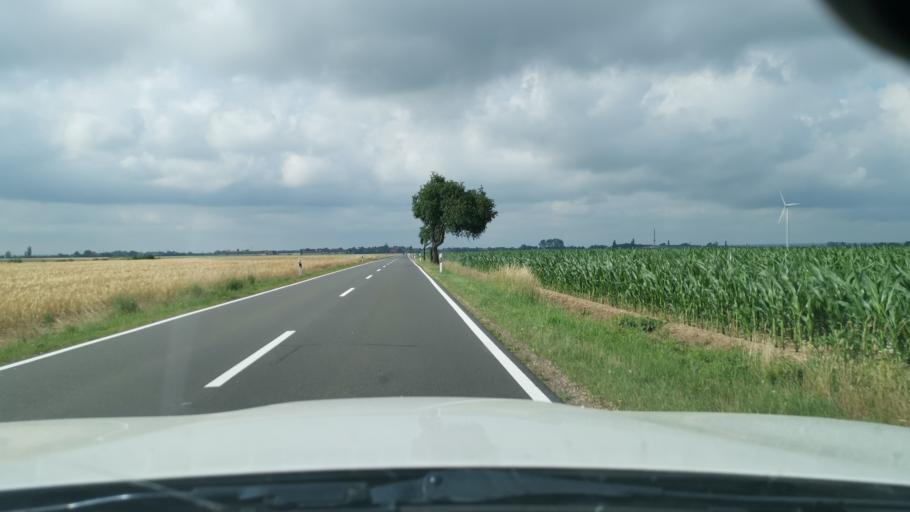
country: DE
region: Saxony-Anhalt
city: Prettin
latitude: 51.6617
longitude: 12.9900
